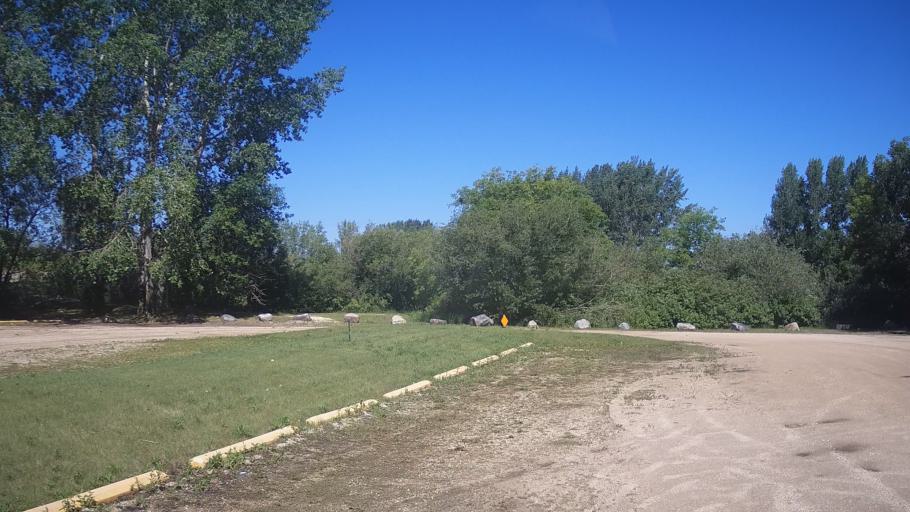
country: CA
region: Manitoba
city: Portage la Prairie
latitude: 49.9476
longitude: -98.3299
